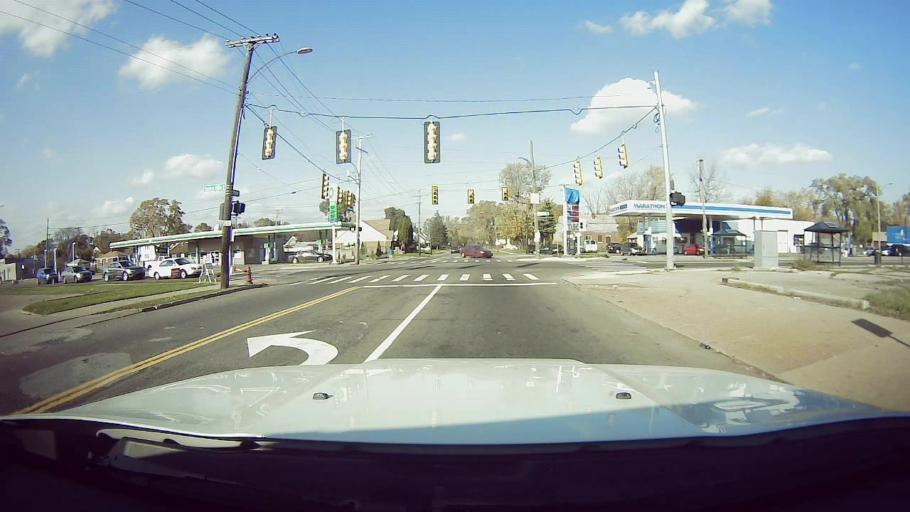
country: US
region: Michigan
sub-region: Wayne County
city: Hamtramck
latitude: 42.4344
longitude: -83.0632
